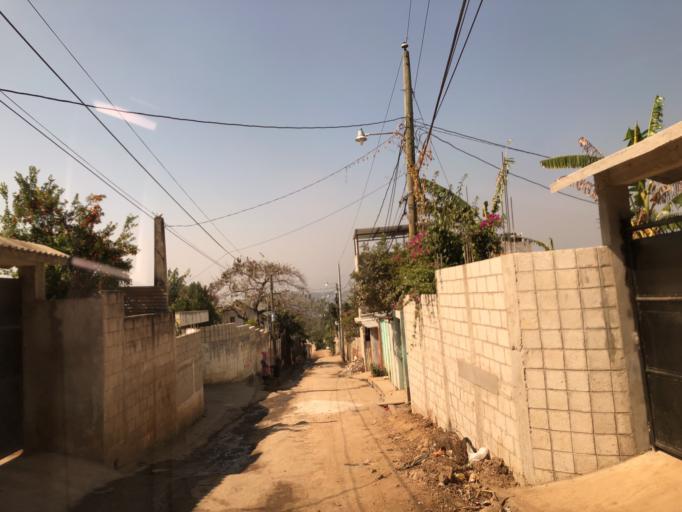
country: GT
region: Guatemala
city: Santa Catarina Pinula
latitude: 14.5365
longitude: -90.5076
